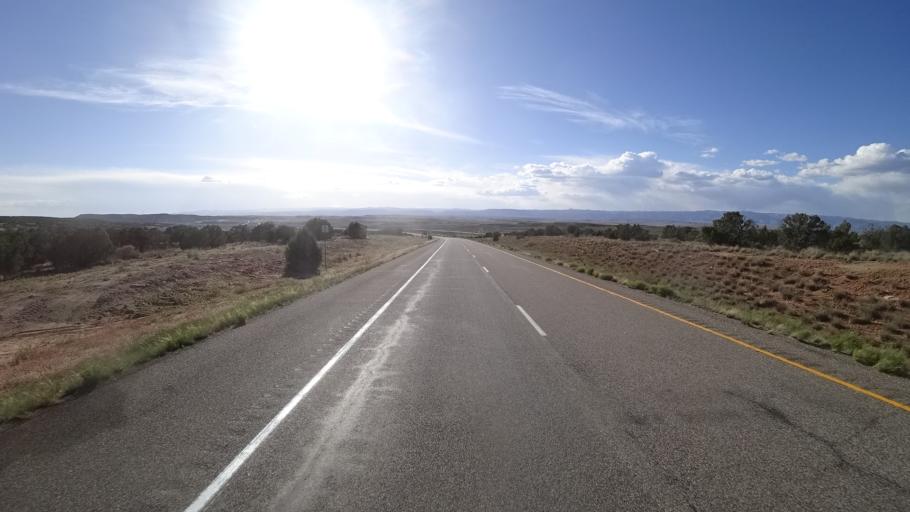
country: US
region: Colorado
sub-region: Mesa County
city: Loma
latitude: 39.1922
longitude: -109.0484
